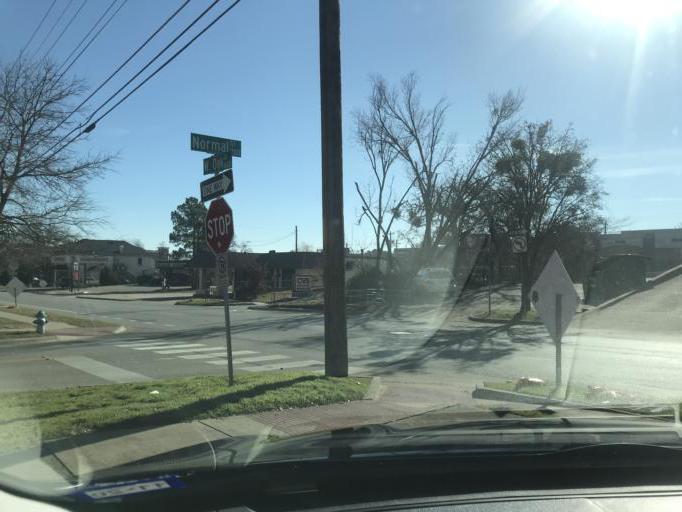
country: US
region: Texas
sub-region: Denton County
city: Denton
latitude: 33.2158
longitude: -97.1493
